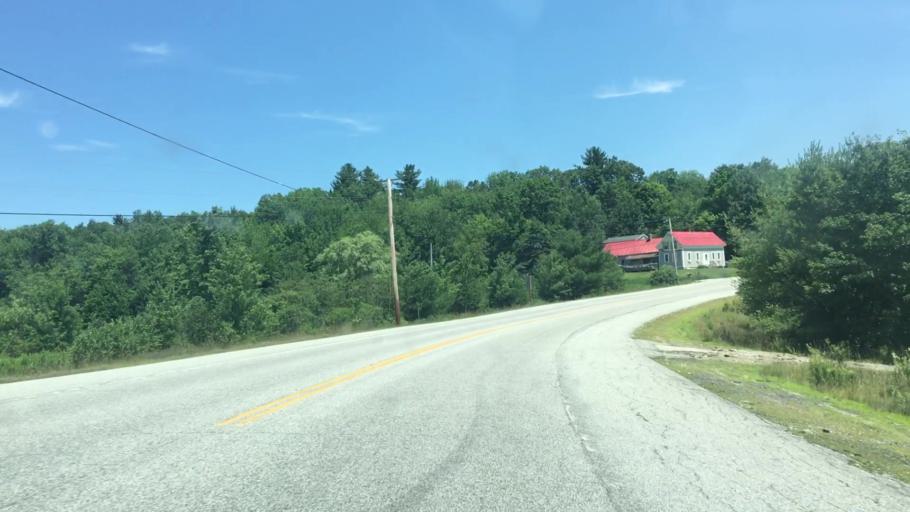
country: US
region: Maine
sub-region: Franklin County
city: Chisholm
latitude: 44.4429
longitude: -70.2159
